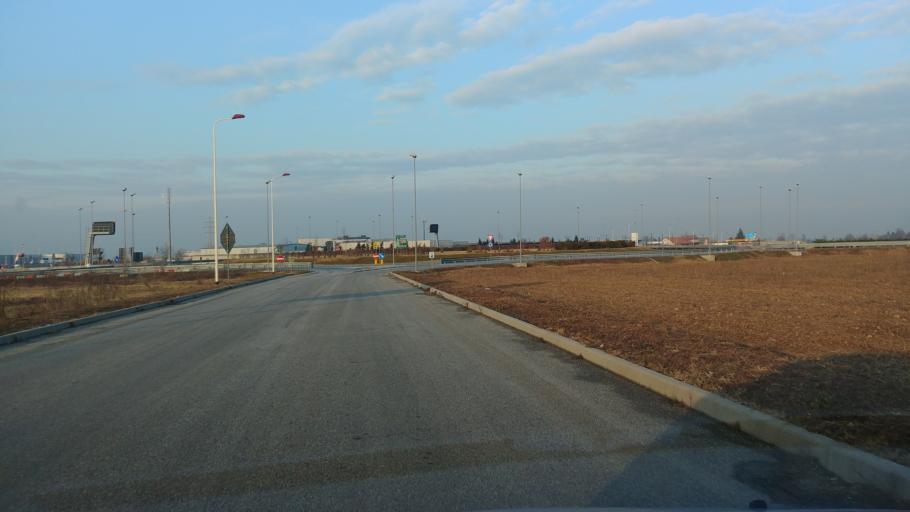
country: IT
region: Piedmont
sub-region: Provincia di Cuneo
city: Cuneo
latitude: 44.4273
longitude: 7.5647
